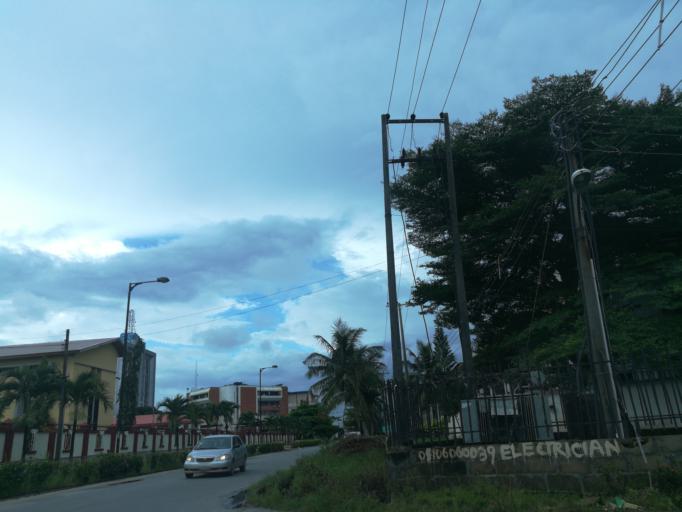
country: NG
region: Lagos
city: Ikoyi
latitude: 6.4443
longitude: 3.4724
